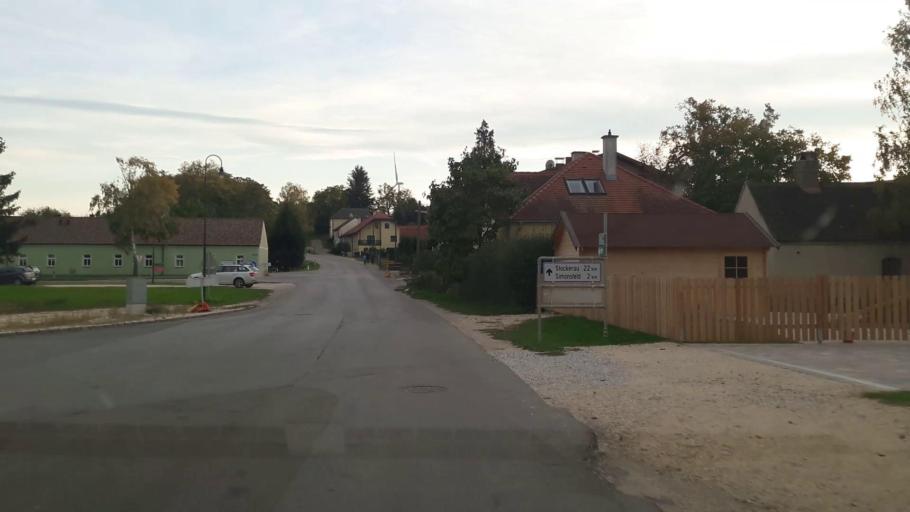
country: AT
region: Lower Austria
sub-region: Politischer Bezirk Korneuburg
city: Ernstbrunn
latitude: 48.5233
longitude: 16.3578
